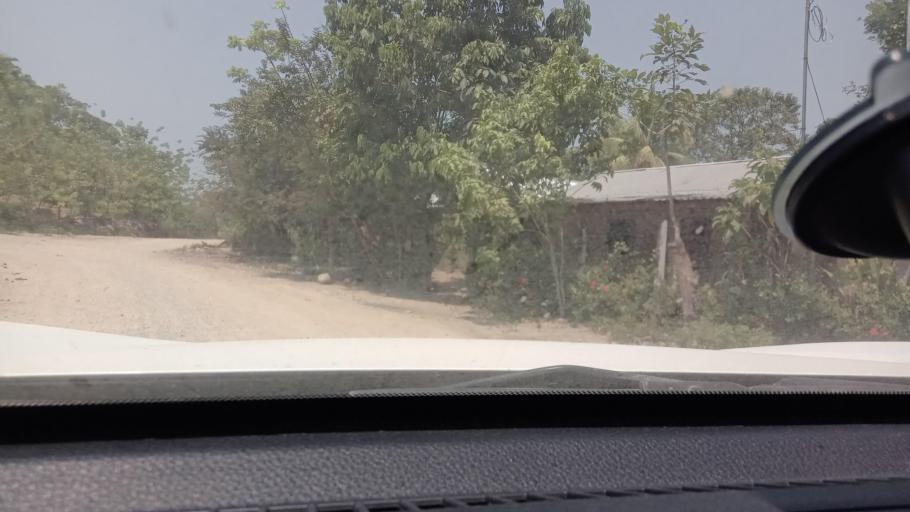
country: MX
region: Tabasco
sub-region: Huimanguillo
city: Francisco Rueda
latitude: 17.4985
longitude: -93.9059
